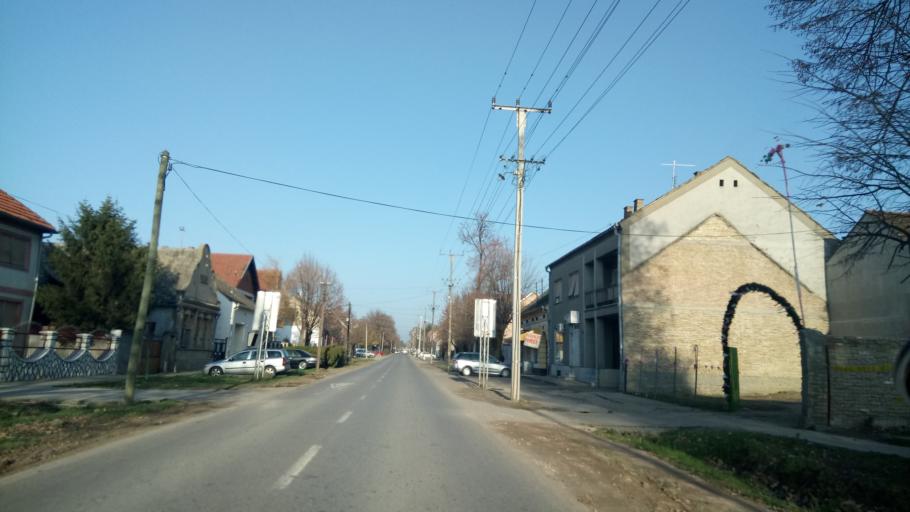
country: RS
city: Novi Slankamen
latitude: 45.1247
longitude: 20.2376
